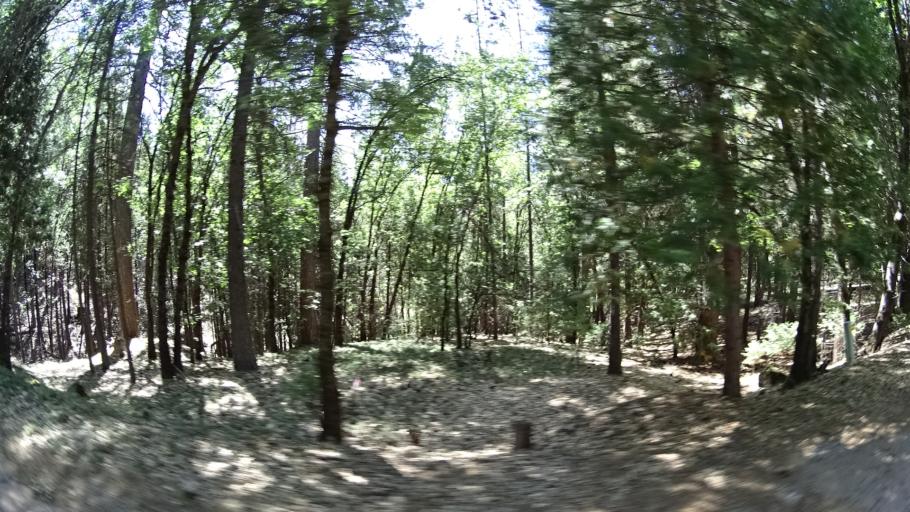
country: US
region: California
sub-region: Amador County
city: Pioneer
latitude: 38.4147
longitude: -120.4947
